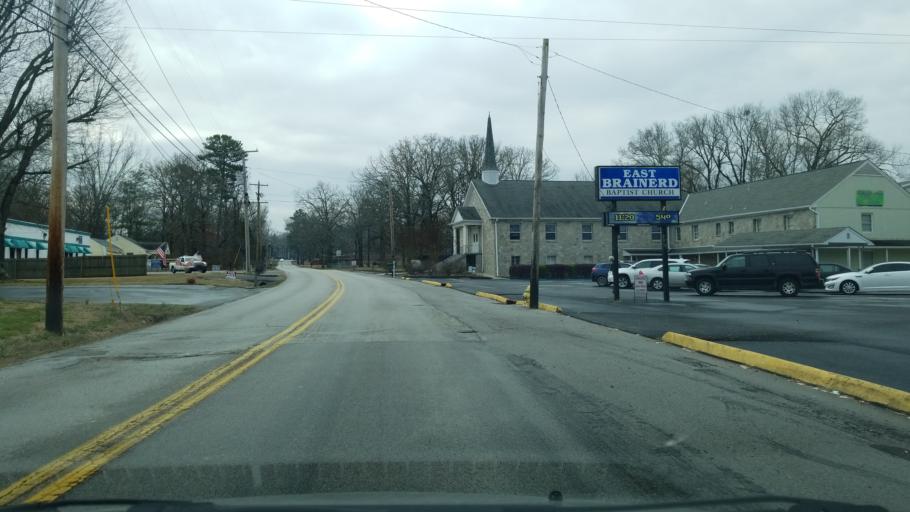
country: US
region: Tennessee
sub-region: Hamilton County
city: East Brainerd
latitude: 35.0019
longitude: -85.1497
